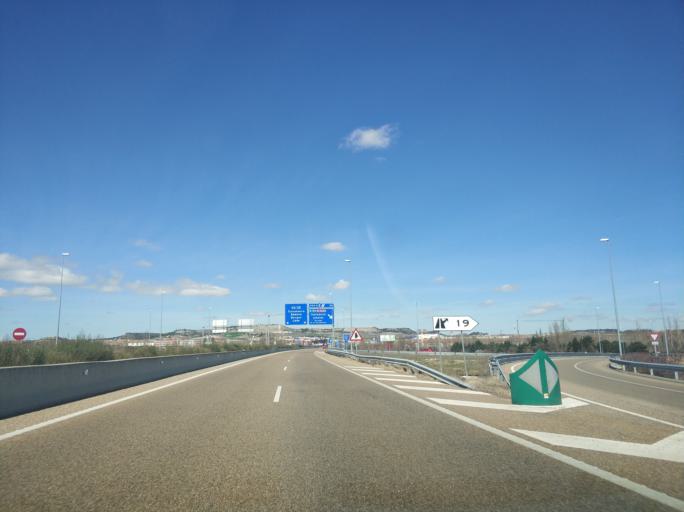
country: ES
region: Castille and Leon
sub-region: Provincia de Valladolid
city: Arroyo
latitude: 41.6048
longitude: -4.7646
